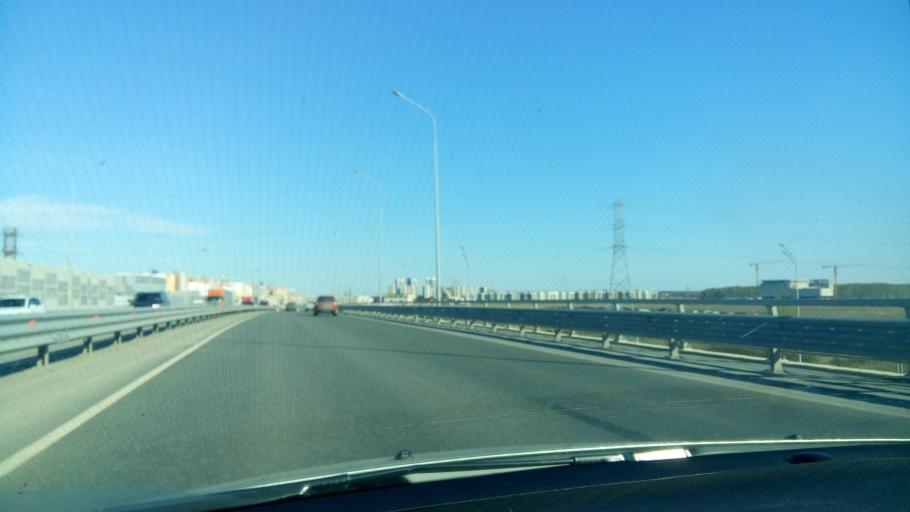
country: RU
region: Tjumen
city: Tyumen
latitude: 57.1134
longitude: 65.5387
